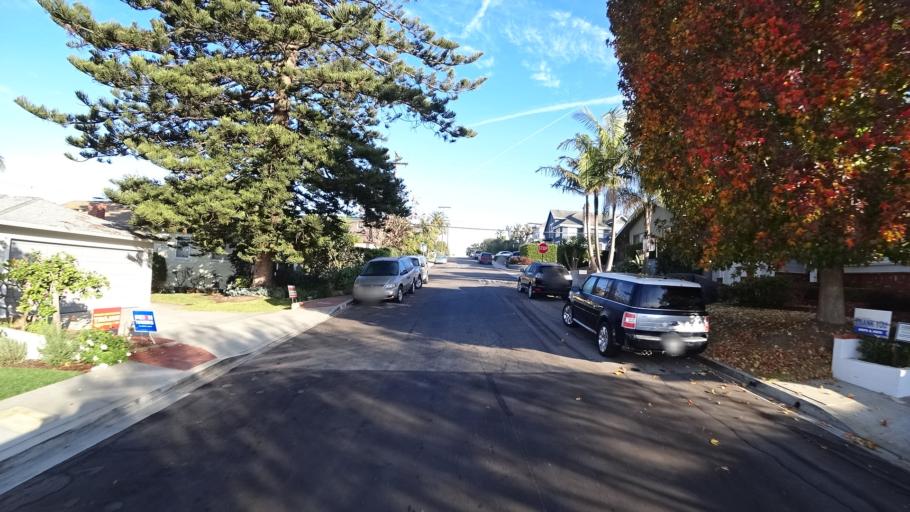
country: US
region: California
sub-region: Los Angeles County
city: Manhattan Beach
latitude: 33.8997
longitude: -118.3990
